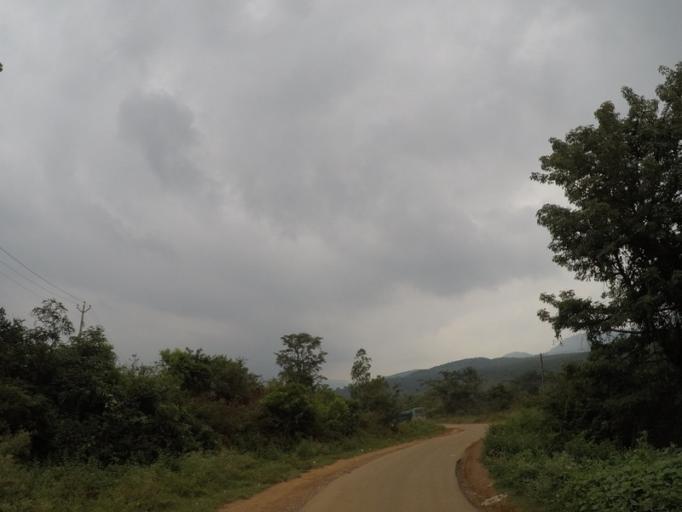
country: IN
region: Karnataka
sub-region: Chikmagalur
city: Tarikere
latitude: 13.5674
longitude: 75.7969
